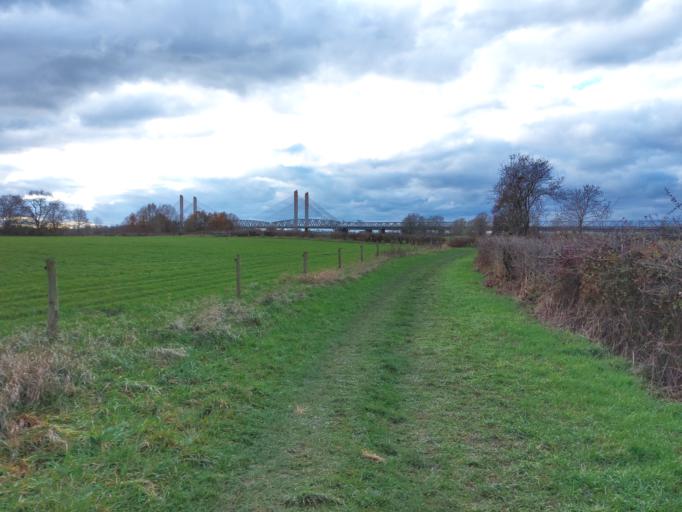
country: NL
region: Gelderland
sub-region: Gemeente Neerijnen
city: Neerijnen
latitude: 51.8244
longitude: 5.2699
